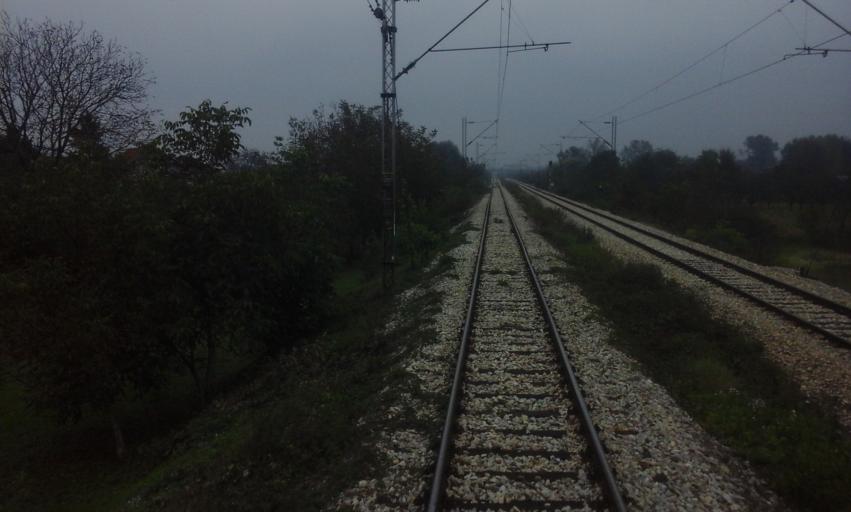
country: RS
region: Central Serbia
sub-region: Pomoravski Okrug
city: Jagodina
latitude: 43.9927
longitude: 21.2430
